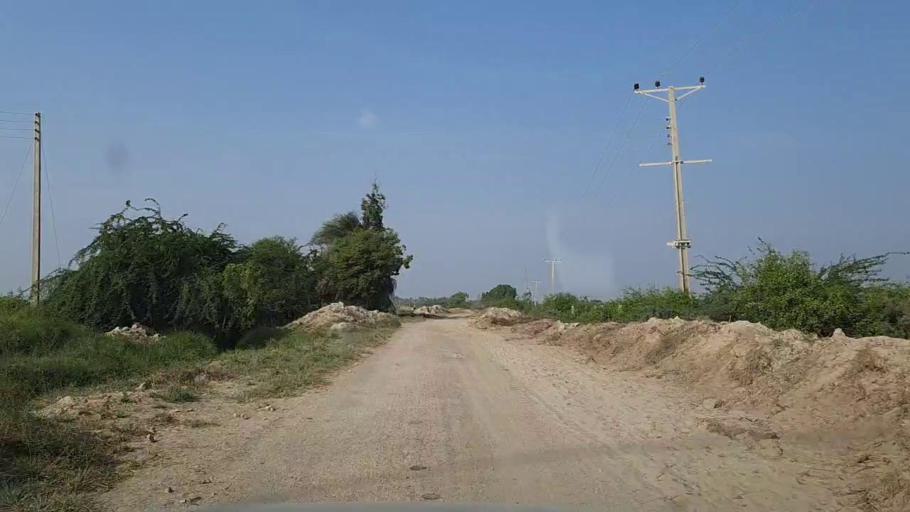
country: PK
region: Sindh
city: Mirpur Sakro
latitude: 24.5828
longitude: 67.5678
